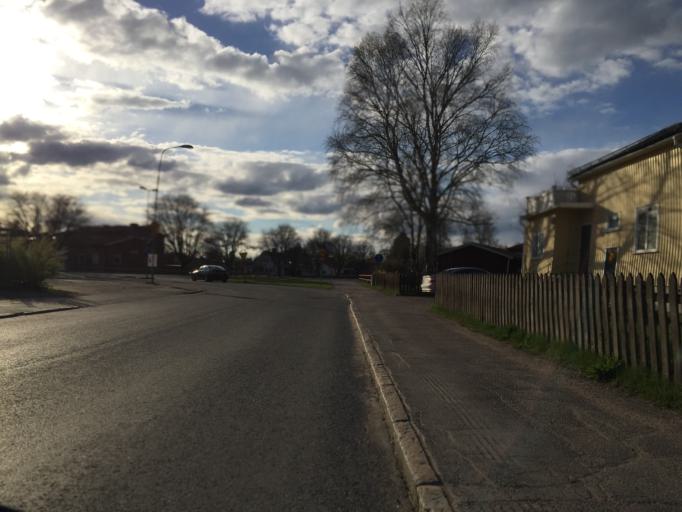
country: SE
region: Dalarna
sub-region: Ludvika Kommun
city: Ludvika
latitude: 60.1266
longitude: 15.1833
